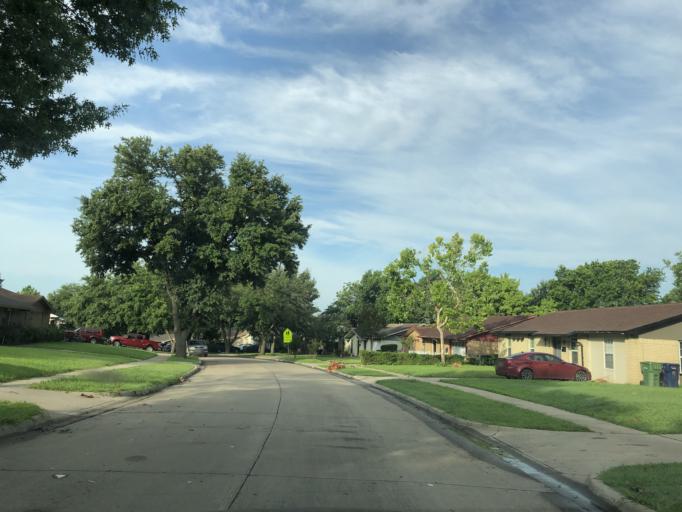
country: US
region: Texas
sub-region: Dallas County
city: Rowlett
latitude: 32.8506
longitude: -96.6019
